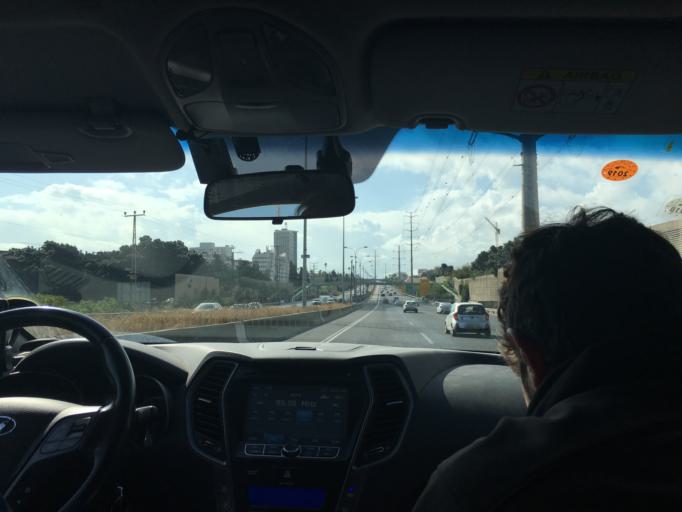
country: IL
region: Tel Aviv
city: Giv`at Shemu'el
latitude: 32.0845
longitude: 34.8457
